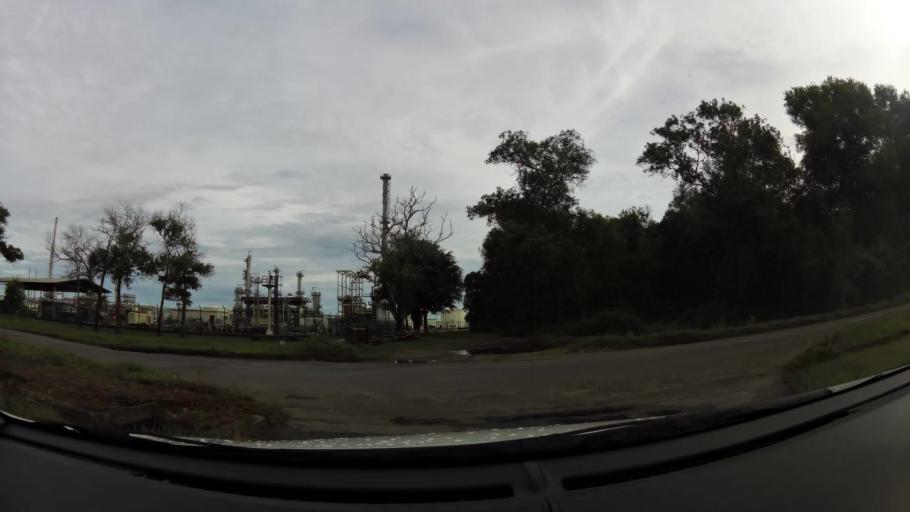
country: BN
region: Belait
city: Seria
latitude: 4.6170
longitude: 114.3459
